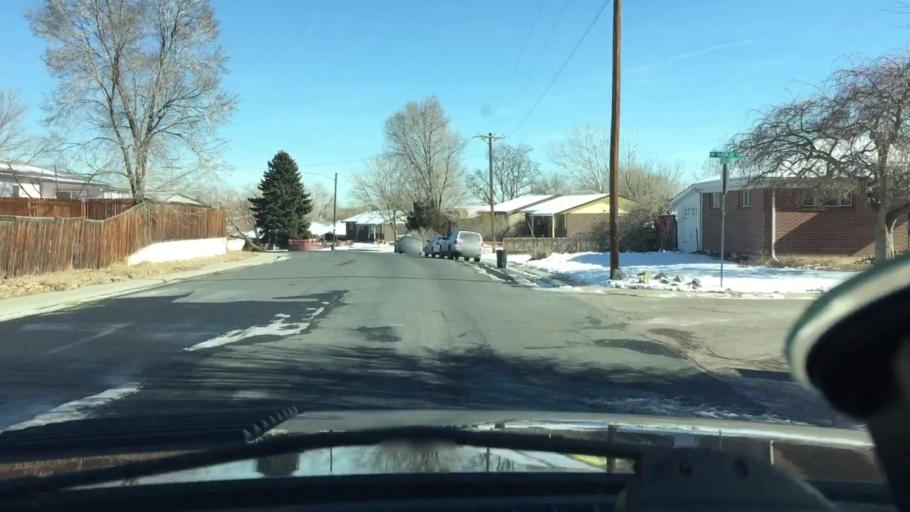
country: US
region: Colorado
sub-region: Adams County
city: Sherrelwood
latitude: 39.8381
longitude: -105.0043
